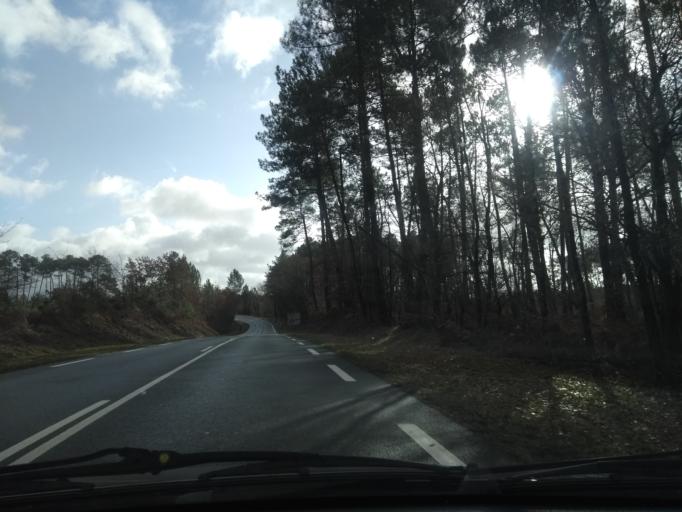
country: FR
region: Aquitaine
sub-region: Departement de la Gironde
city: Salles
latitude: 44.5365
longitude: -0.8423
